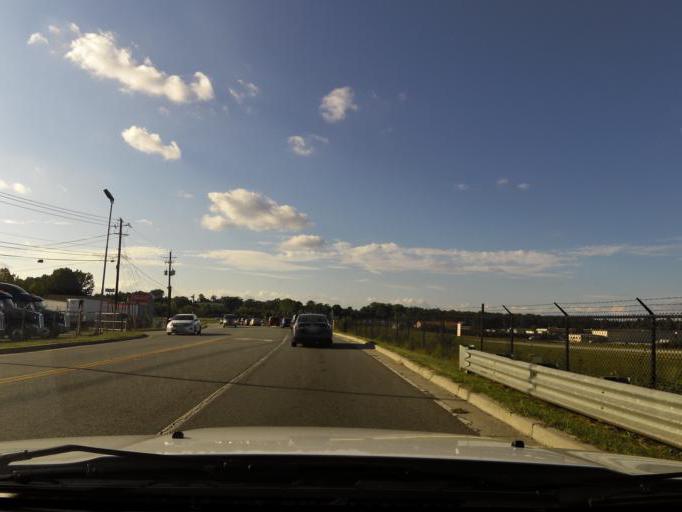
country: US
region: Georgia
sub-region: Cobb County
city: Kennesaw
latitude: 34.0111
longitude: -84.6066
